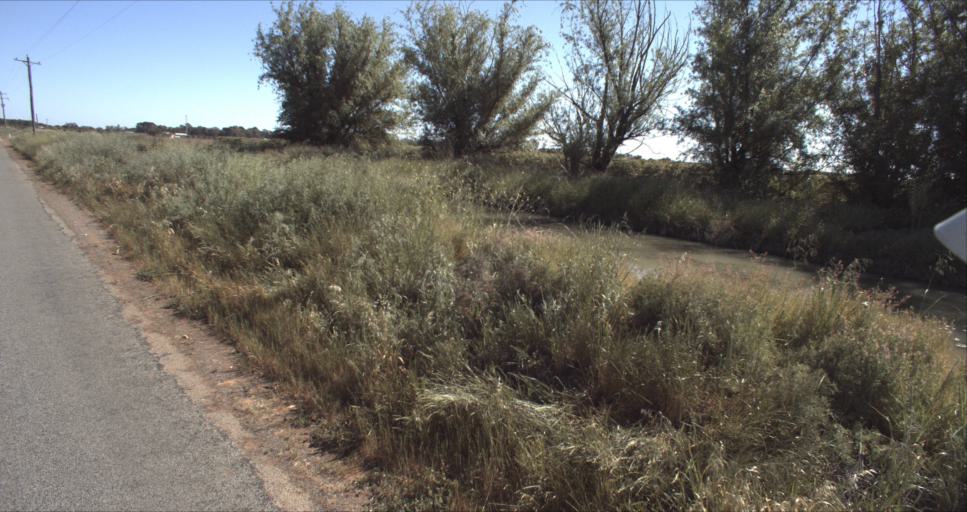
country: AU
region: New South Wales
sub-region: Leeton
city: Leeton
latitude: -34.5415
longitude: 146.3418
